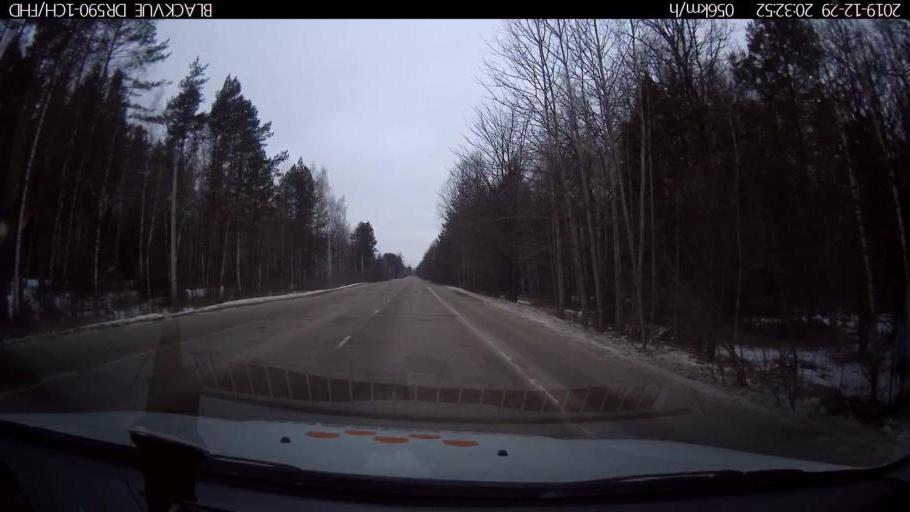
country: RU
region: Nizjnij Novgorod
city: Afonino
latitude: 56.1773
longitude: 44.0587
